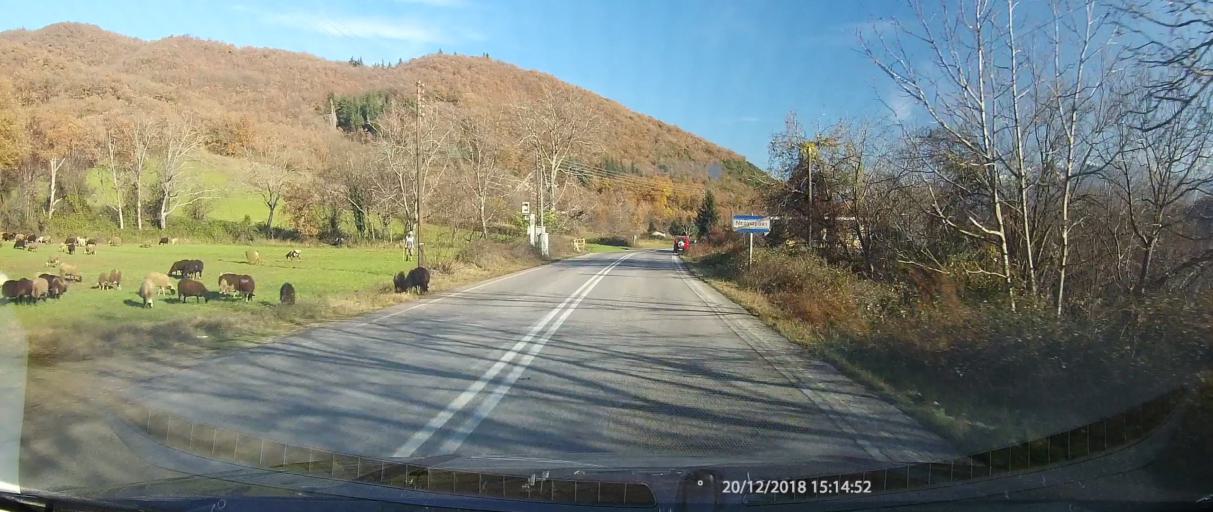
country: GR
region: Central Greece
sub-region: Nomos Fthiotidos
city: Makrakomi
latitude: 38.9318
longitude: 21.9833
